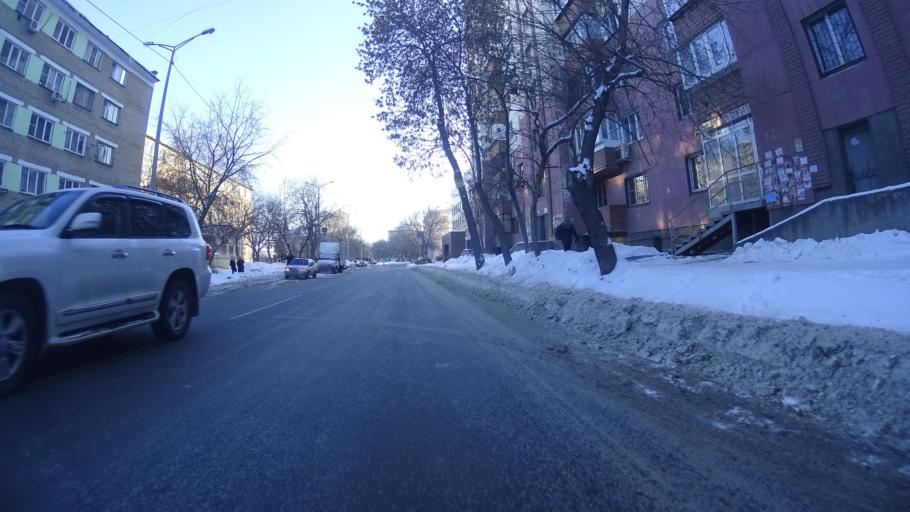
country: RU
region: Chelyabinsk
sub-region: Gorod Chelyabinsk
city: Chelyabinsk
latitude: 55.1503
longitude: 61.4176
